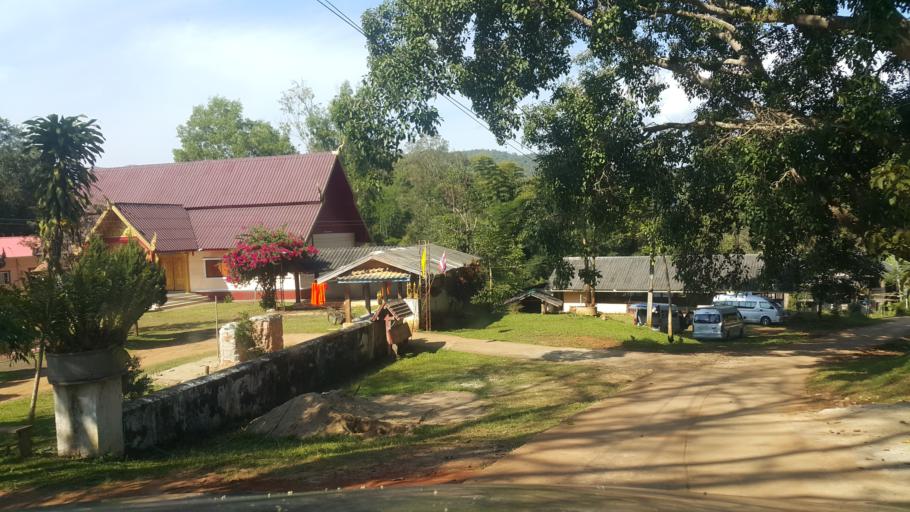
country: TH
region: Chiang Mai
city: Samoeng
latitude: 18.9495
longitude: 98.6745
